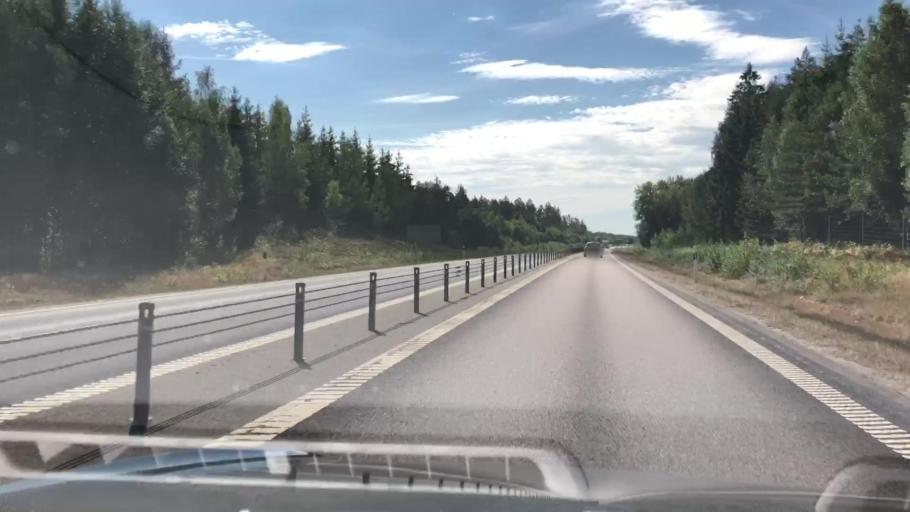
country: SE
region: Kalmar
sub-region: Torsas Kommun
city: Torsas
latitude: 56.5109
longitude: 16.0862
